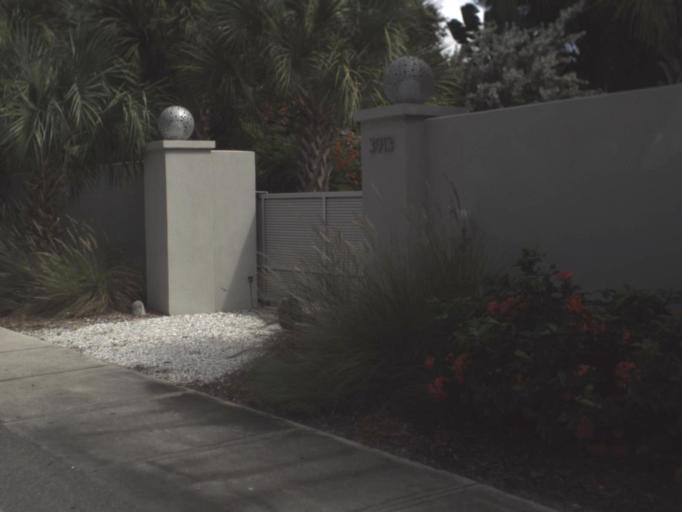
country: US
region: Florida
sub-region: Sarasota County
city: Siesta Key
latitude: 27.2986
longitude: -82.5579
